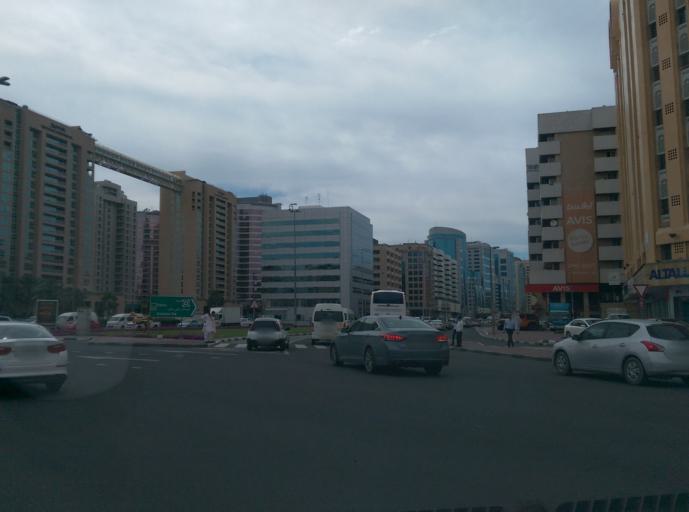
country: AE
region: Ash Shariqah
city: Sharjah
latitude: 25.2590
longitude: 55.3264
